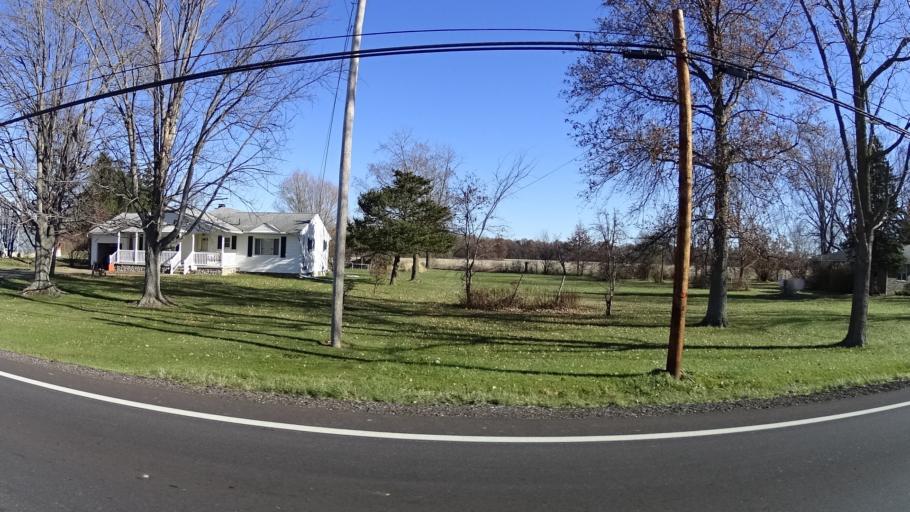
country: US
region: Ohio
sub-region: Lorain County
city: Lagrange
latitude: 41.2914
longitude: -82.1180
